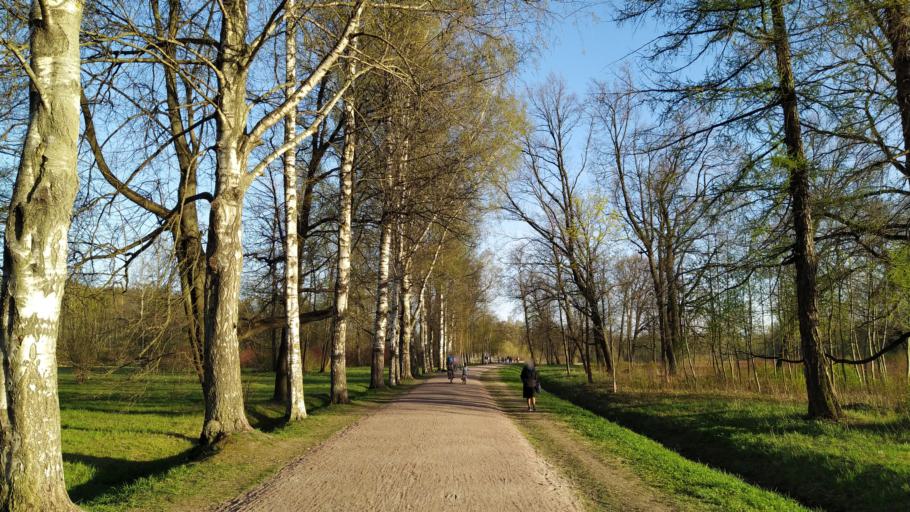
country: RU
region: St.-Petersburg
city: Pavlovsk
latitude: 59.7083
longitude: 30.4245
